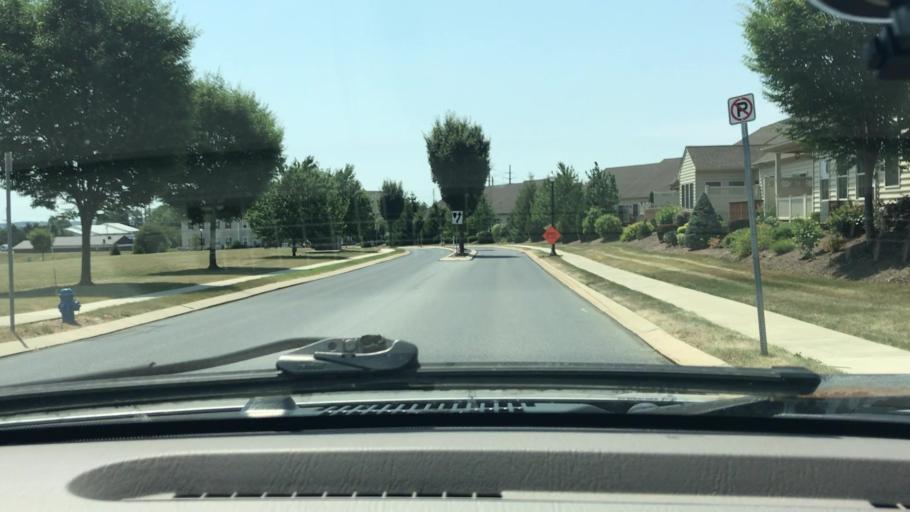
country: US
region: Pennsylvania
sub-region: Lancaster County
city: Mount Joy
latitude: 40.1123
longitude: -76.4830
